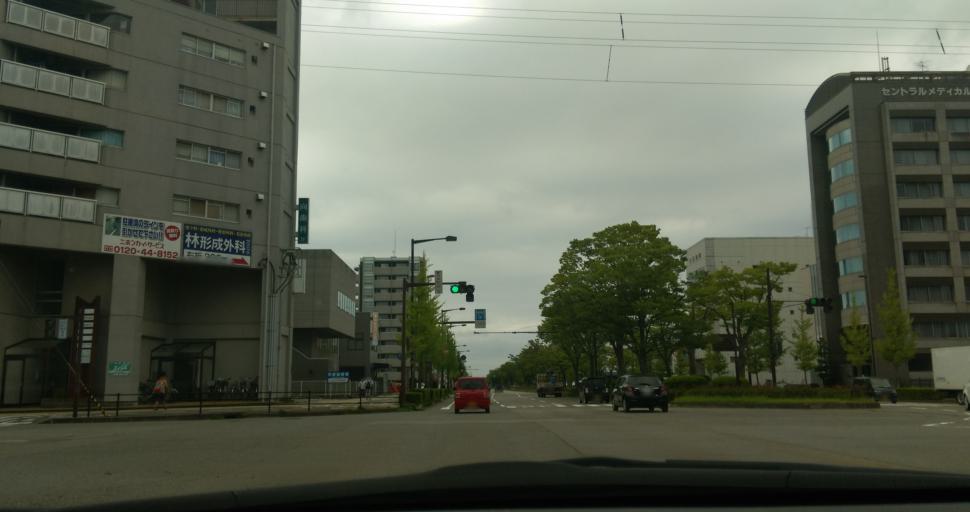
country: JP
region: Ishikawa
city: Kanazawa-shi
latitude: 36.5853
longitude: 136.6374
